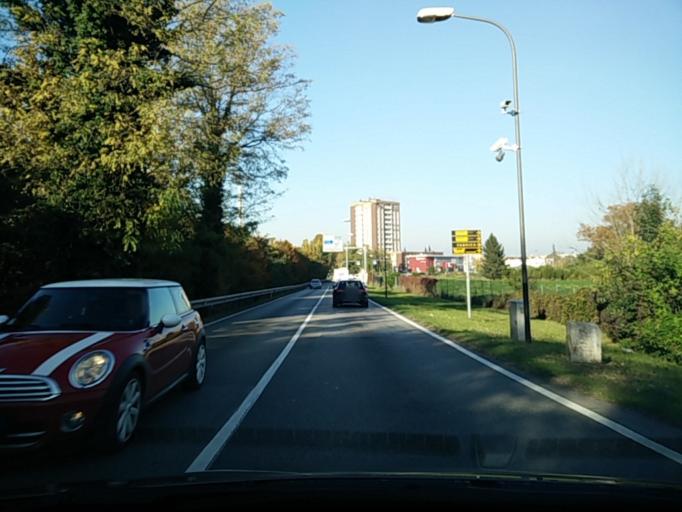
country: IT
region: Veneto
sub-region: Provincia di Treviso
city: Treviso
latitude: 45.6656
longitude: 12.2225
